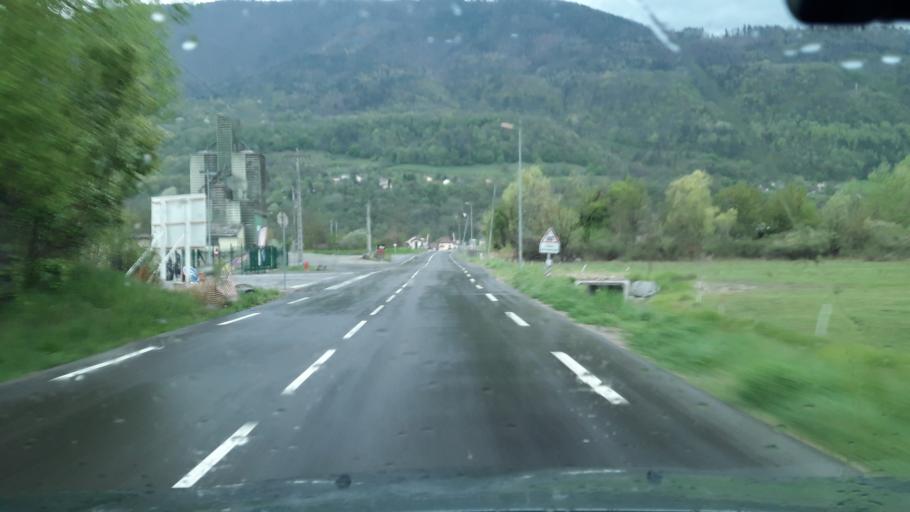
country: FR
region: Rhone-Alpes
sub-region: Departement de l'Isere
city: Le Cheylas
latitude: 45.3943
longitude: 5.9952
